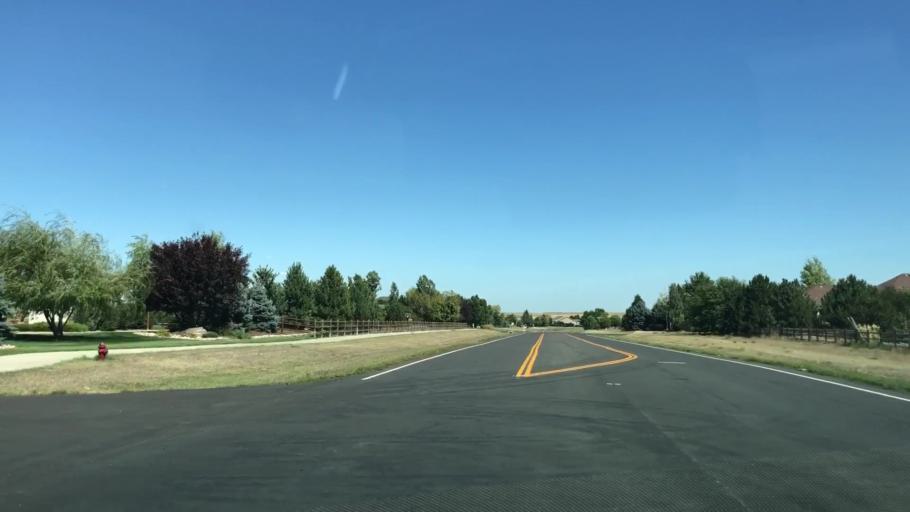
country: US
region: Colorado
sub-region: Weld County
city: Windsor
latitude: 40.4434
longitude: -104.9554
